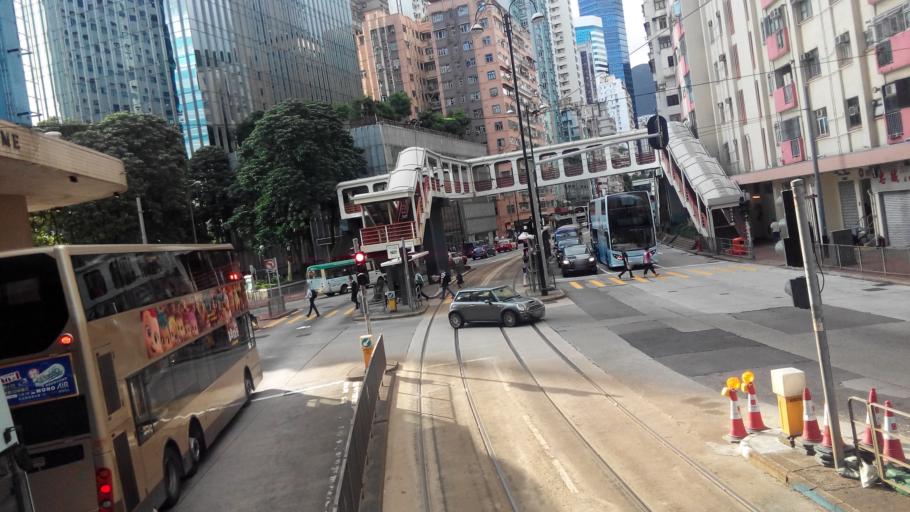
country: HK
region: Kowloon City
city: Kowloon
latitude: 22.2909
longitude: 114.2089
